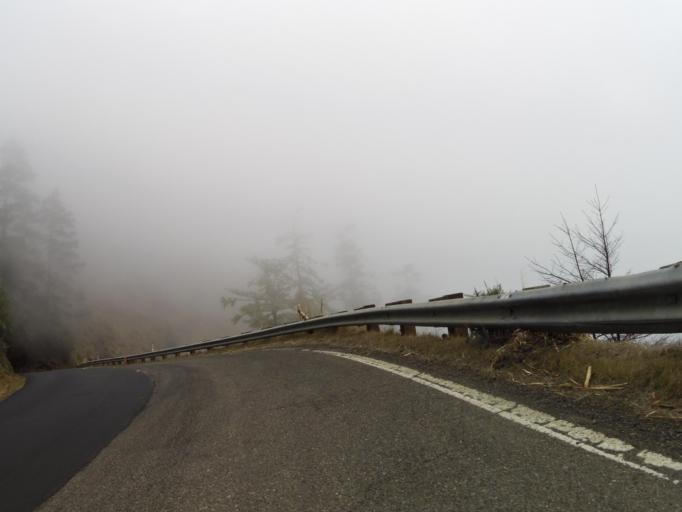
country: US
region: California
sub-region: Sonoma County
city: Monte Rio
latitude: 38.4975
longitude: -123.2038
